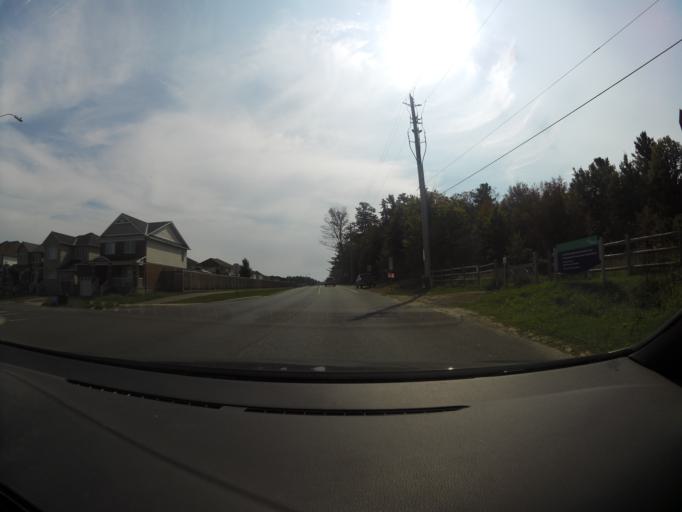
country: CA
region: Ontario
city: Bells Corners
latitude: 45.3464
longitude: -75.9465
